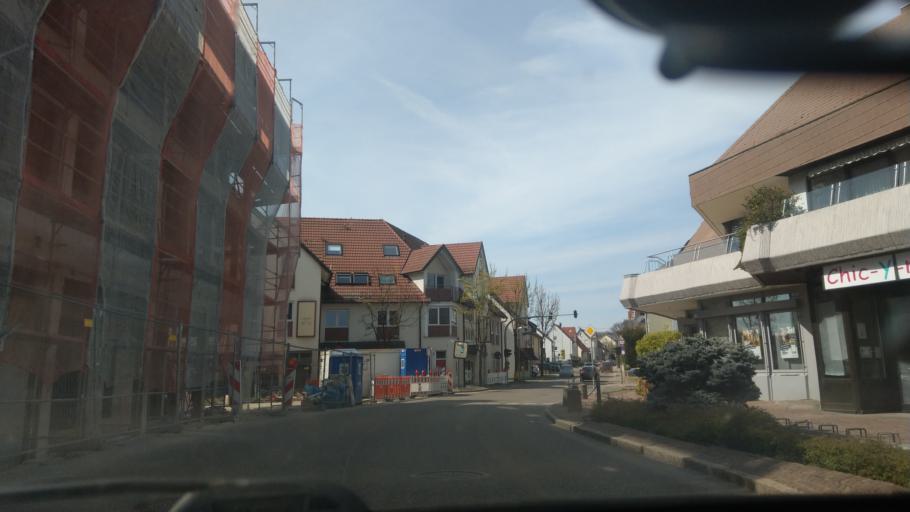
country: DE
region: Baden-Wuerttemberg
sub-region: Regierungsbezirk Stuttgart
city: Wolfschlugen
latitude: 48.6536
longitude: 9.2875
